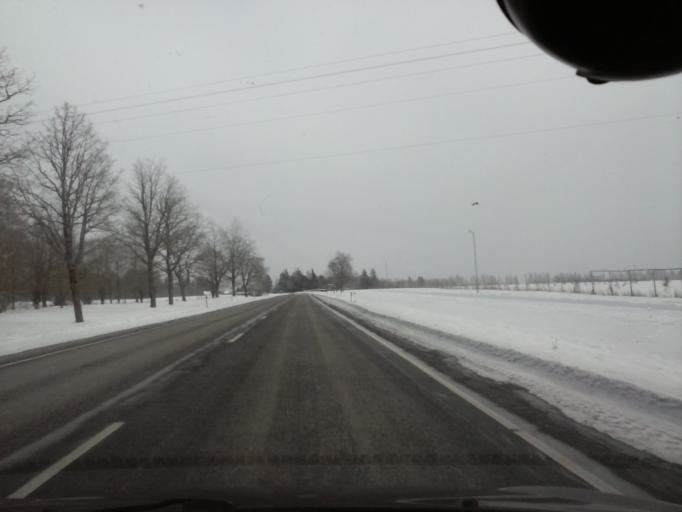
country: EE
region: Viljandimaa
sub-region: Viljandi linn
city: Viljandi
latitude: 58.3473
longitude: 25.5113
